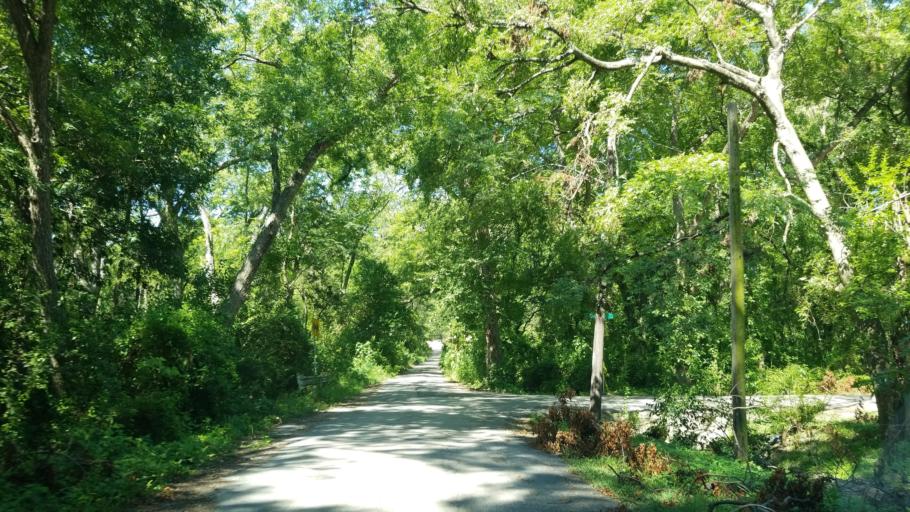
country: US
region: Texas
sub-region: Dallas County
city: Dallas
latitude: 32.7306
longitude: -96.7882
